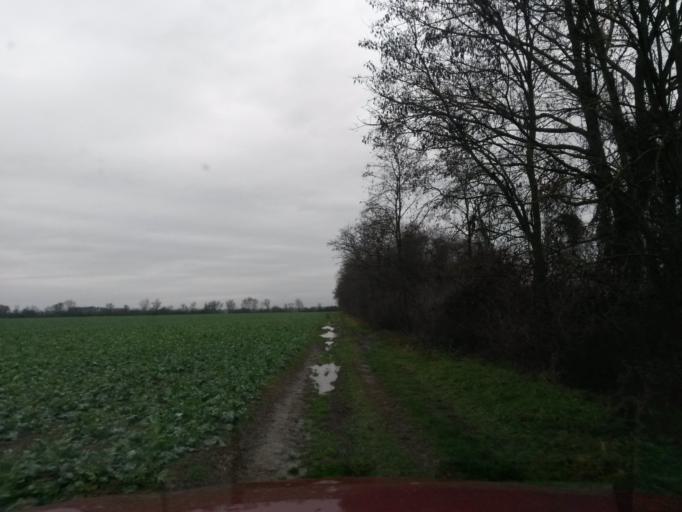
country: SK
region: Kosicky
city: Sobrance
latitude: 48.6376
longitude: 22.0881
